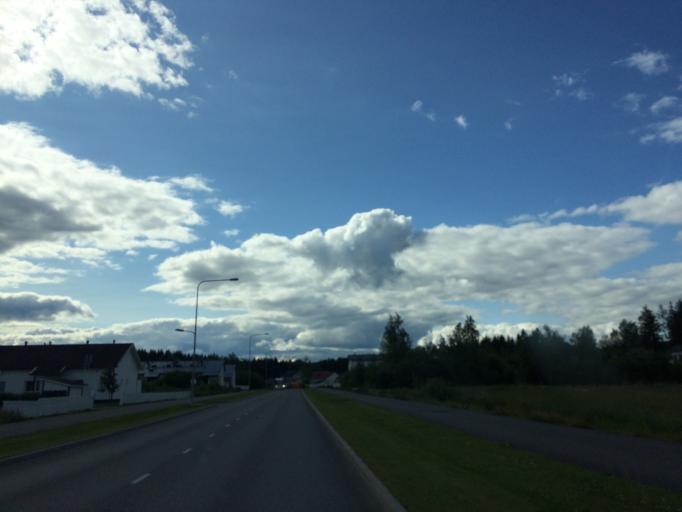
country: FI
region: Haeme
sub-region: Haemeenlinna
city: Parola
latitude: 60.9770
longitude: 24.3748
